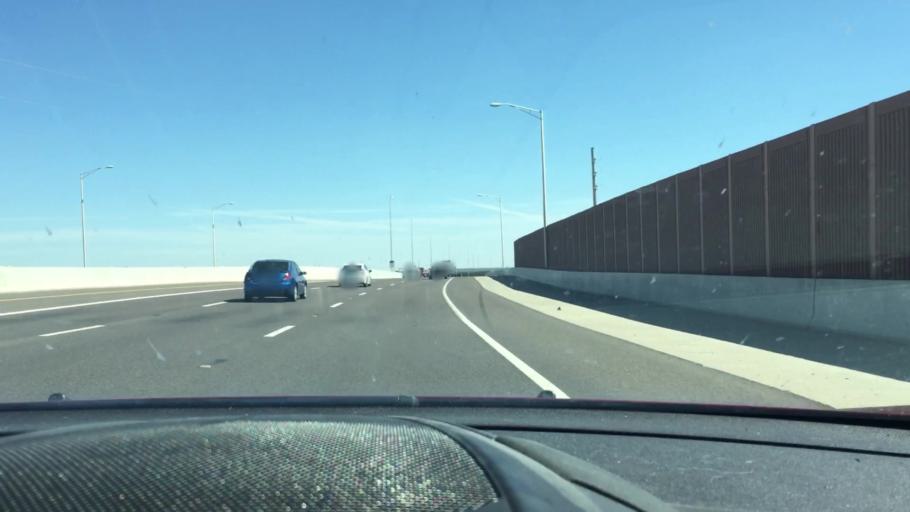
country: US
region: Arizona
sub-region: Maricopa County
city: Fountain Hills
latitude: 33.4718
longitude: -111.6843
